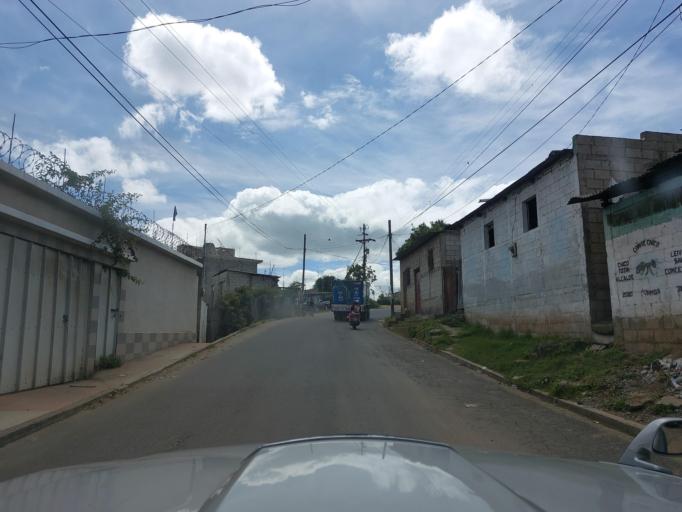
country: GT
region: Chimaltenango
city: San Andres Itzapa
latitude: 14.6204
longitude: -90.8356
